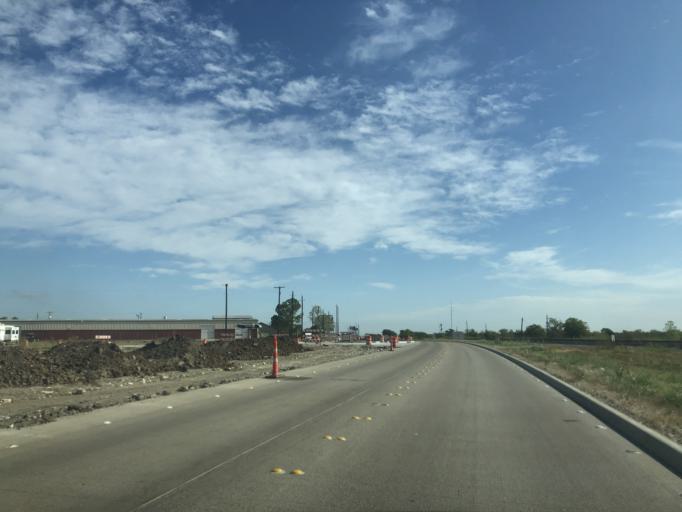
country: US
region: Texas
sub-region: Denton County
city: Justin
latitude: 33.0568
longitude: -97.2997
